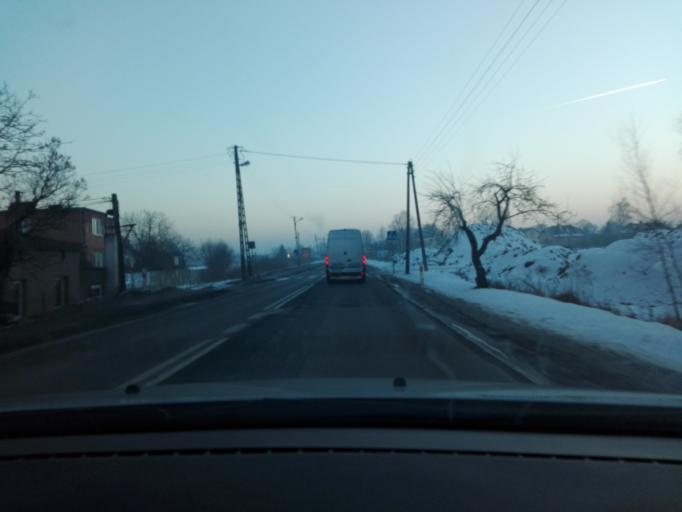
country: PL
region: Lodz Voivodeship
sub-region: Powiat zgierski
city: Zgierz
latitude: 51.8752
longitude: 19.4096
